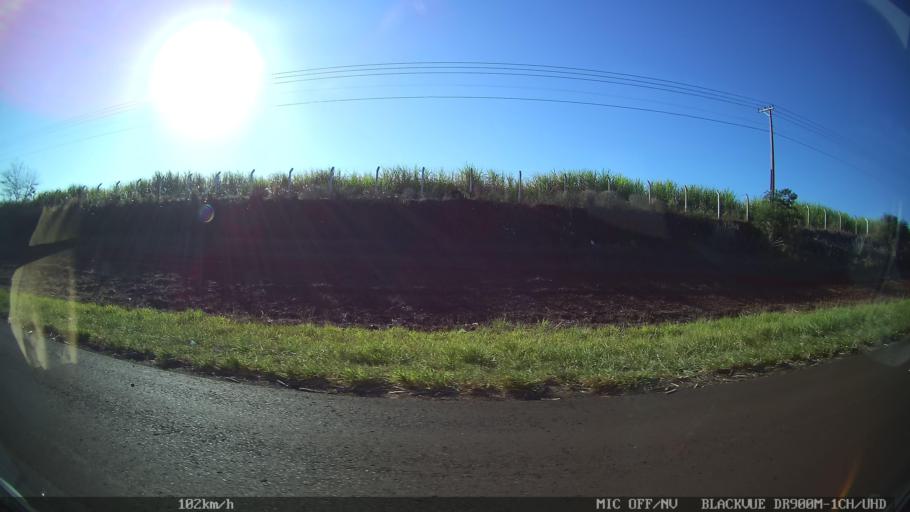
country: BR
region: Sao Paulo
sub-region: Olimpia
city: Olimpia
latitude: -20.7206
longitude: -49.0160
